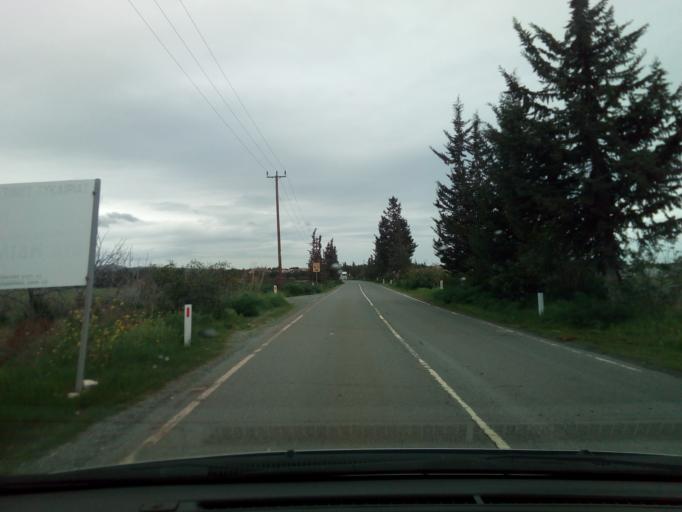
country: CY
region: Larnaka
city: Kofinou
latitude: 34.7263
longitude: 33.3226
